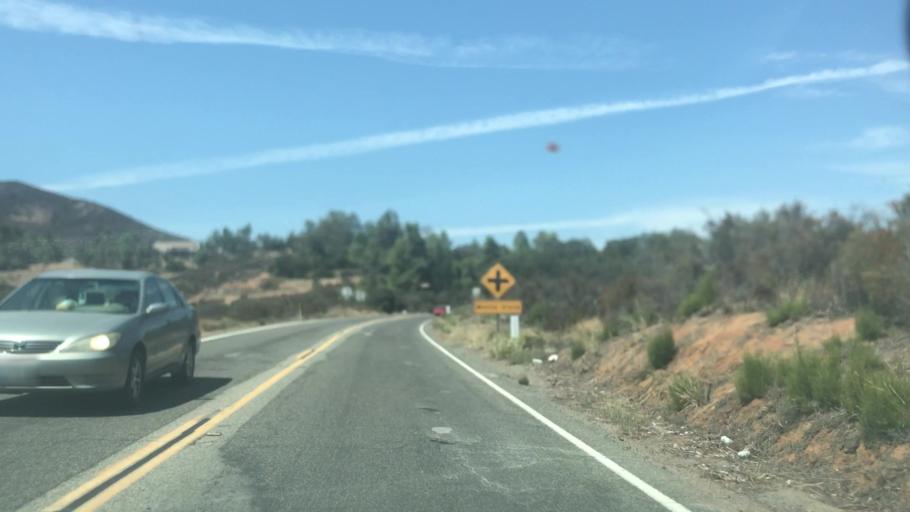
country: US
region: California
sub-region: Riverside County
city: Lakeland Village
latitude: 33.6431
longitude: -117.4208
